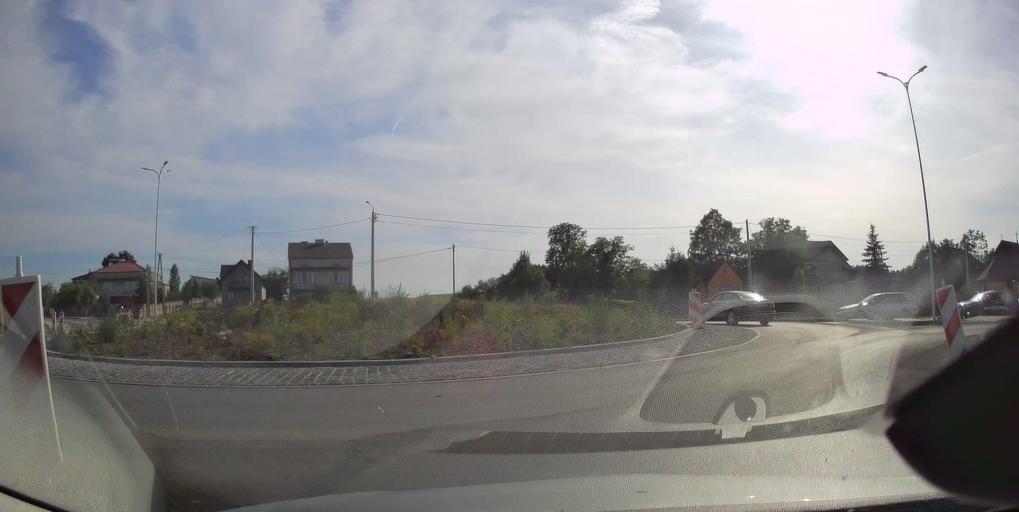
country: PL
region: Swietokrzyskie
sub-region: Powiat konecki
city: Radoszyce
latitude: 51.0713
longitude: 20.2685
